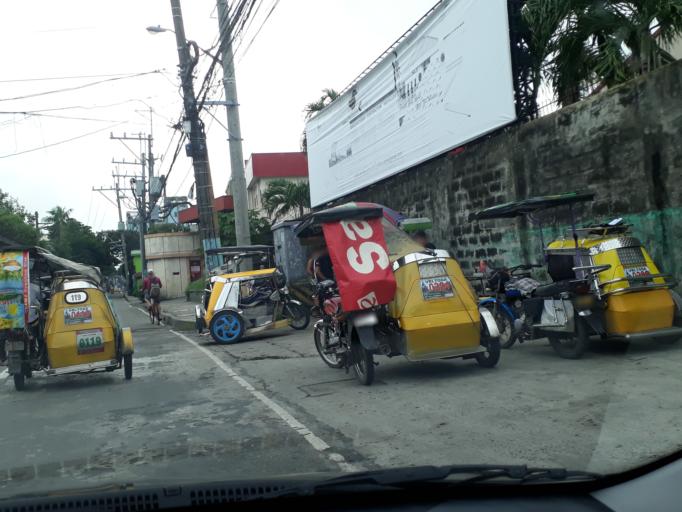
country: PH
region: Calabarzon
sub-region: Province of Rizal
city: Valenzuela
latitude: 14.7110
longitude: 120.9648
